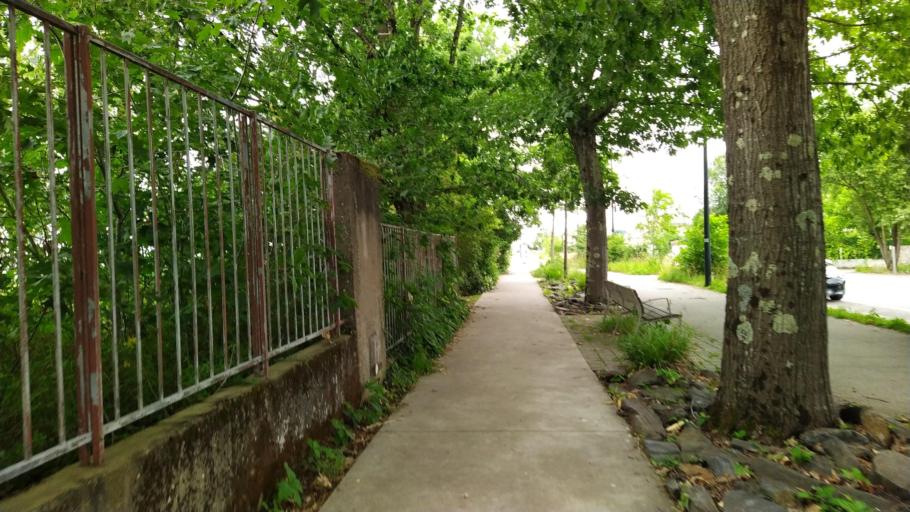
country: FR
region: Pays de la Loire
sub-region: Departement de la Loire-Atlantique
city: Sainte-Luce-sur-Loire
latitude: 47.2371
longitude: -1.5079
